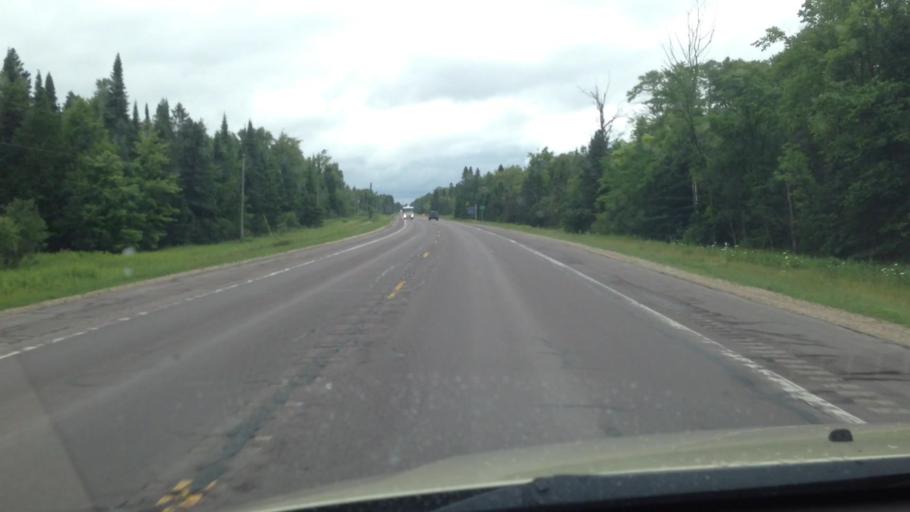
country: US
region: Michigan
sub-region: Schoolcraft County
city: Manistique
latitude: 46.0619
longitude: -85.9585
